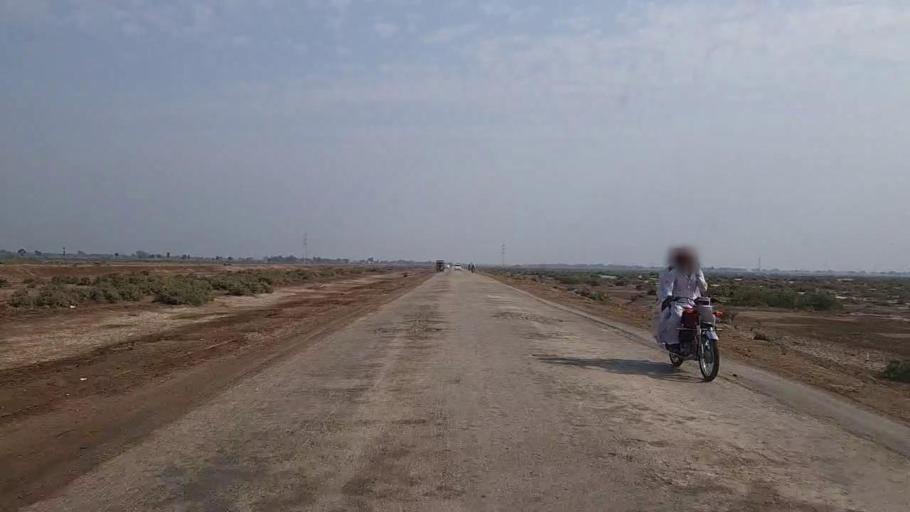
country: PK
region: Sindh
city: Mirpur Khas
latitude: 25.4233
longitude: 69.0225
